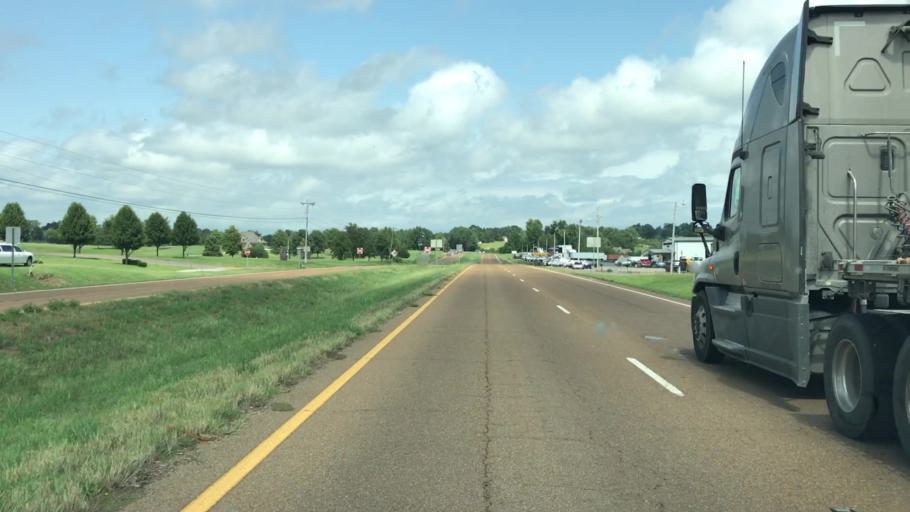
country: US
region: Tennessee
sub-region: Obion County
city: Englewood
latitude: 36.3498
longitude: -89.1455
